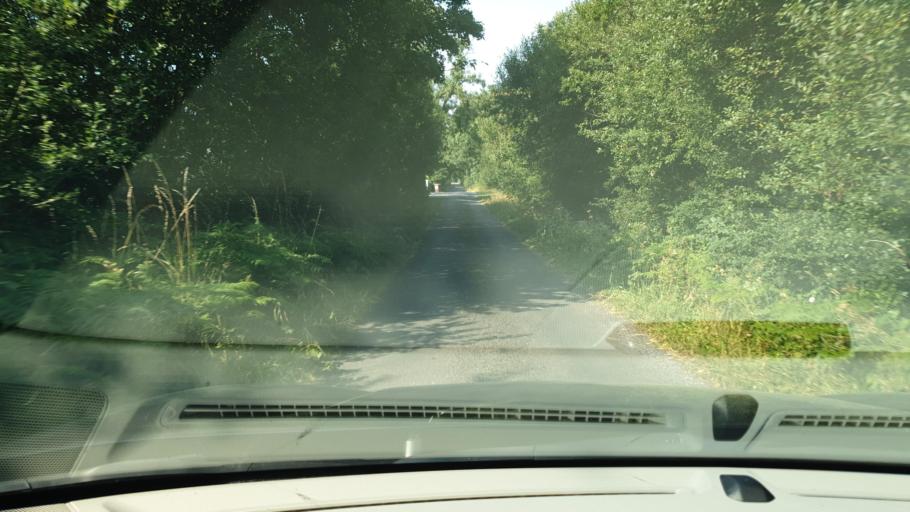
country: IE
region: Leinster
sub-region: An Mhi
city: Athboy
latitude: 53.6127
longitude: -6.9925
